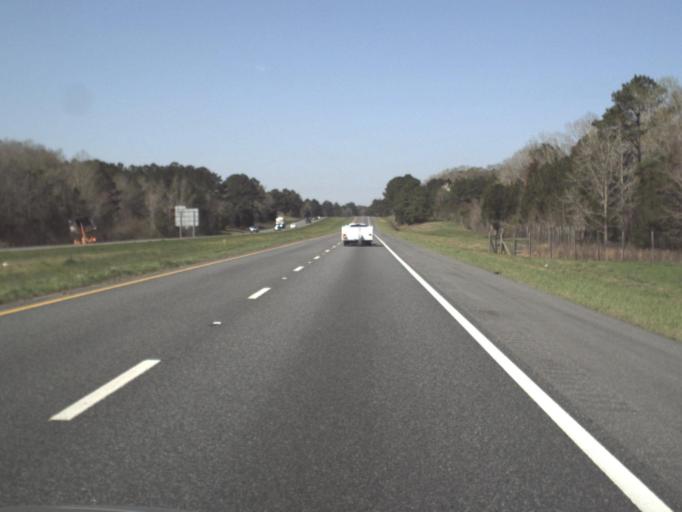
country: US
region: Florida
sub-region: Jackson County
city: Marianna
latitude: 30.7265
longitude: -85.2086
